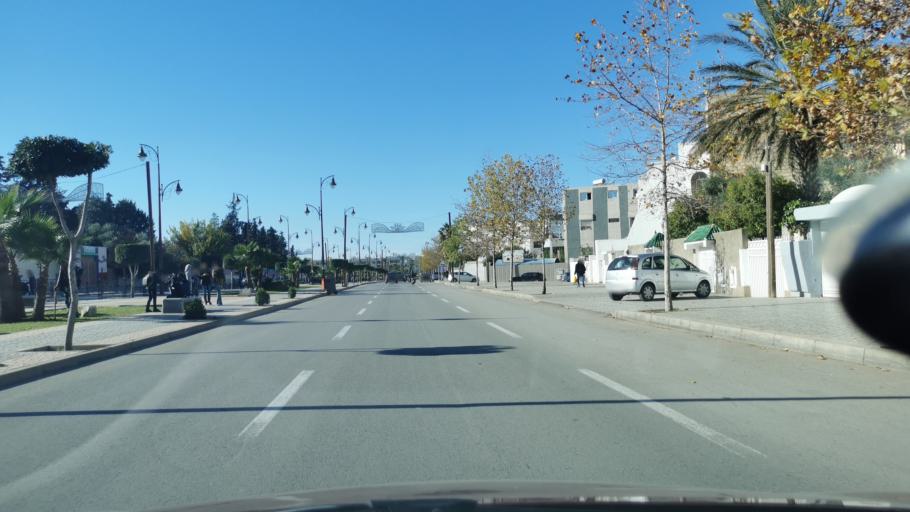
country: MA
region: Fes-Boulemane
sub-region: Fes
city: Fes
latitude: 34.0158
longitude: -5.0145
